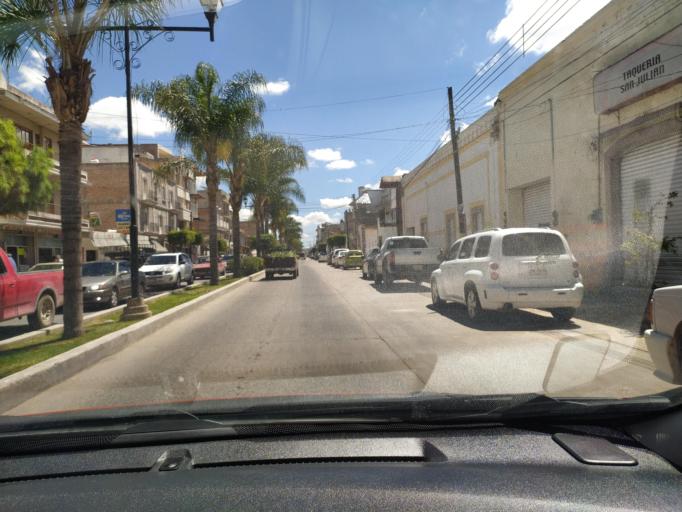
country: MX
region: Jalisco
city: San Julian
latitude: 21.0105
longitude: -102.1791
